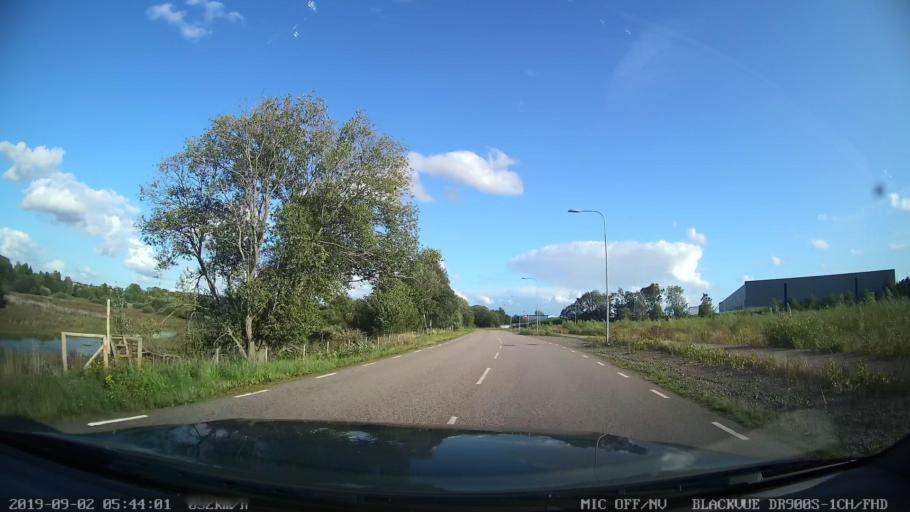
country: SE
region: Skane
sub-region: Helsingborg
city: Odakra
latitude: 56.0776
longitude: 12.7453
